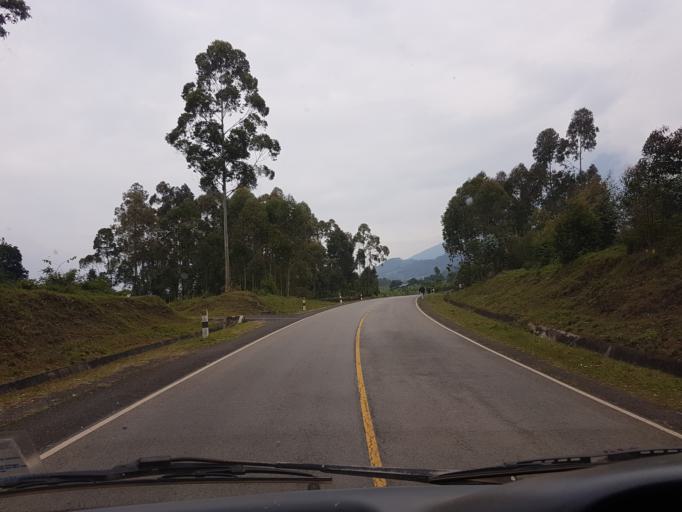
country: UG
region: Western Region
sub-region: Kisoro District
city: Kisoro
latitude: -1.3255
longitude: 29.7294
